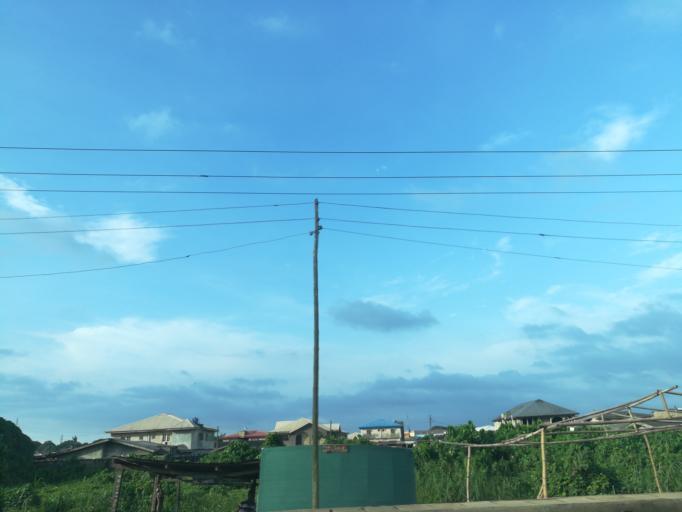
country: NG
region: Lagos
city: Ebute Ikorodu
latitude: 6.6135
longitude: 3.4786
